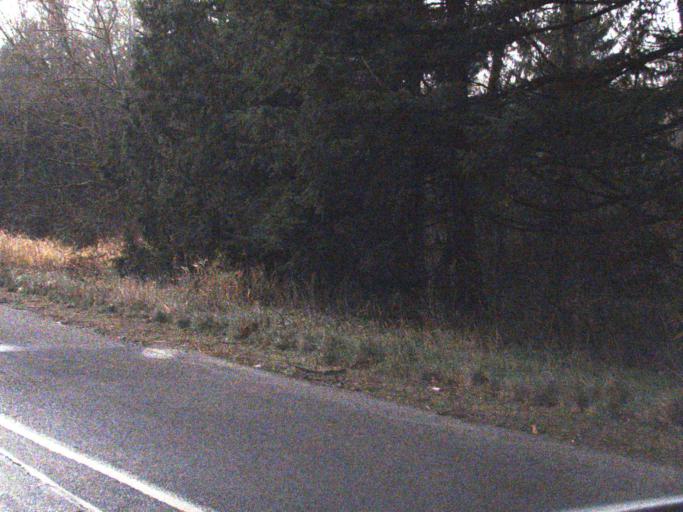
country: US
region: Washington
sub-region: Whatcom County
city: Sudden Valley
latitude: 48.6441
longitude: -122.3644
